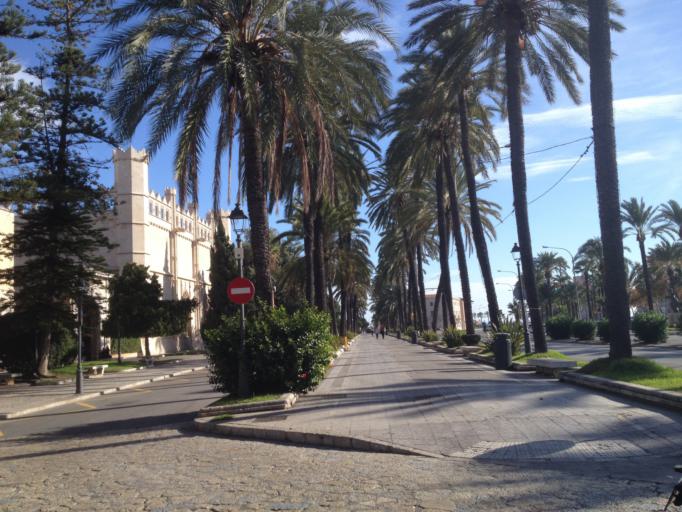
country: ES
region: Balearic Islands
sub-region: Illes Balears
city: Palma
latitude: 39.5686
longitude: 2.6432
